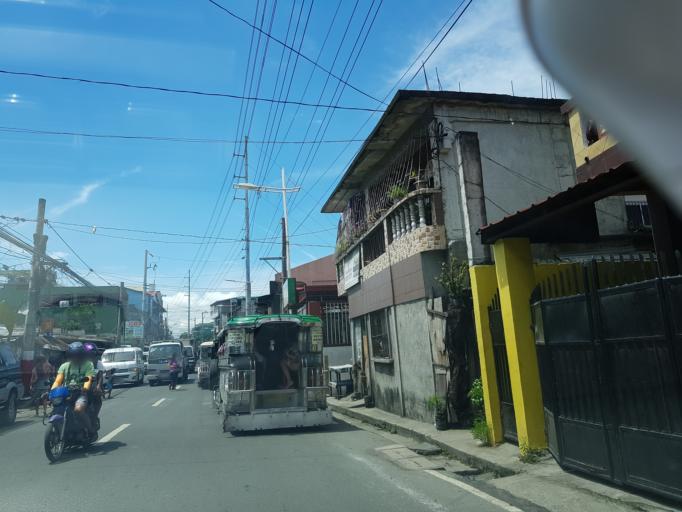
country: PH
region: Calabarzon
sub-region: Province of Rizal
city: Taguig
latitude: 14.4972
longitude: 121.0624
